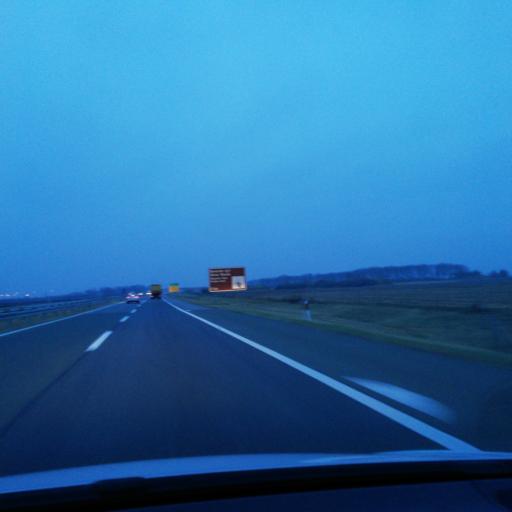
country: RS
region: Autonomna Pokrajina Vojvodina
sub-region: Sremski Okrug
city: Ruma
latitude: 44.9659
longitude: 19.7947
